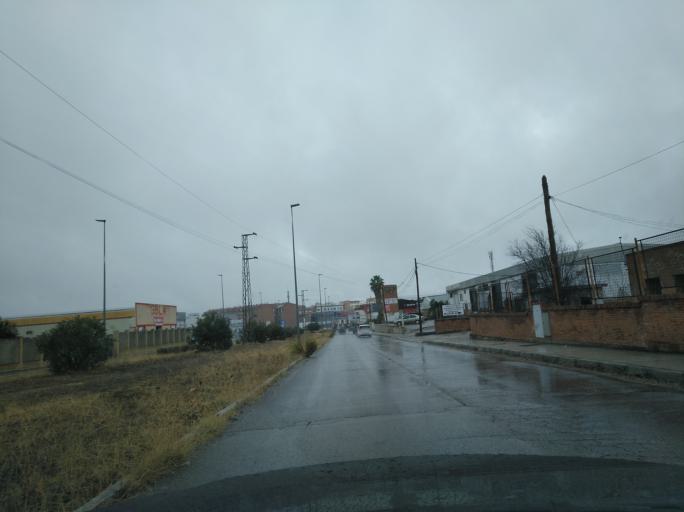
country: ES
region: Extremadura
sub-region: Provincia de Badajoz
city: Badajoz
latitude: 38.8922
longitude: -6.9926
